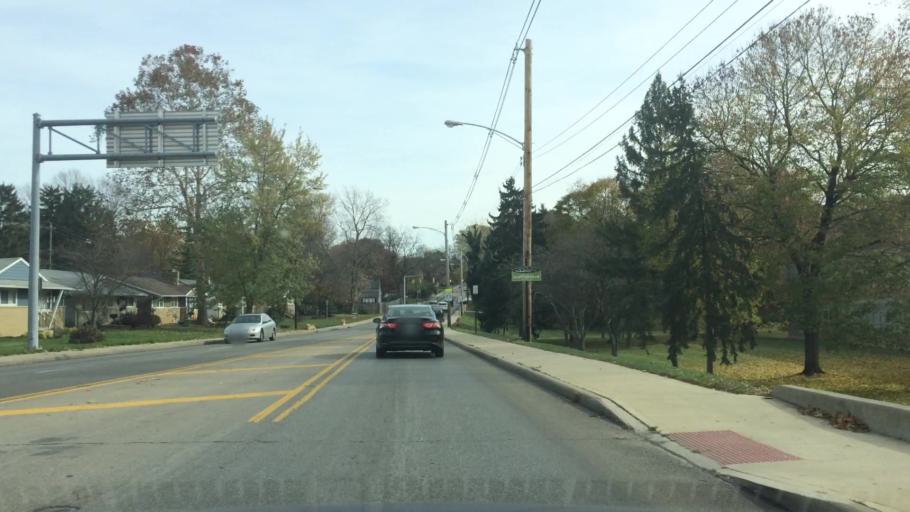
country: US
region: Ohio
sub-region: Franklin County
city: Worthington
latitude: 40.0518
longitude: -83.0303
